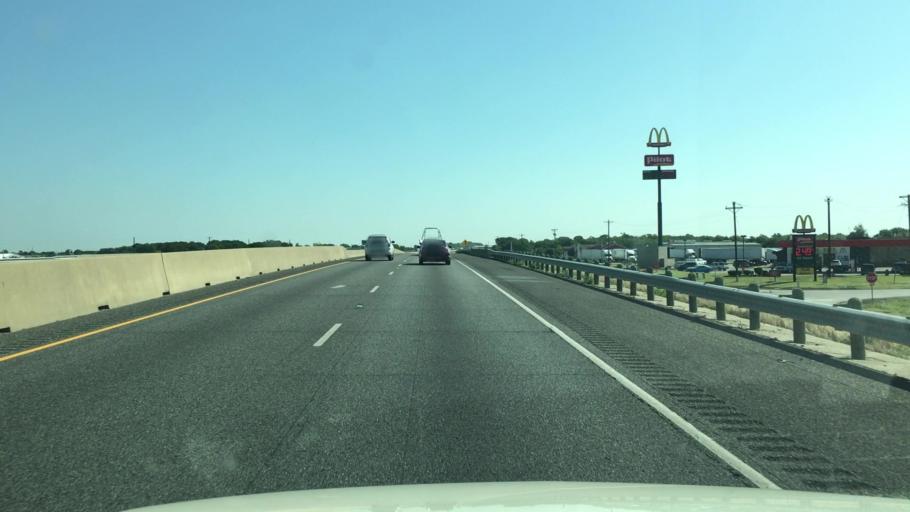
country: US
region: Texas
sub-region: Hunt County
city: Caddo Mills
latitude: 33.0427
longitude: -96.1800
